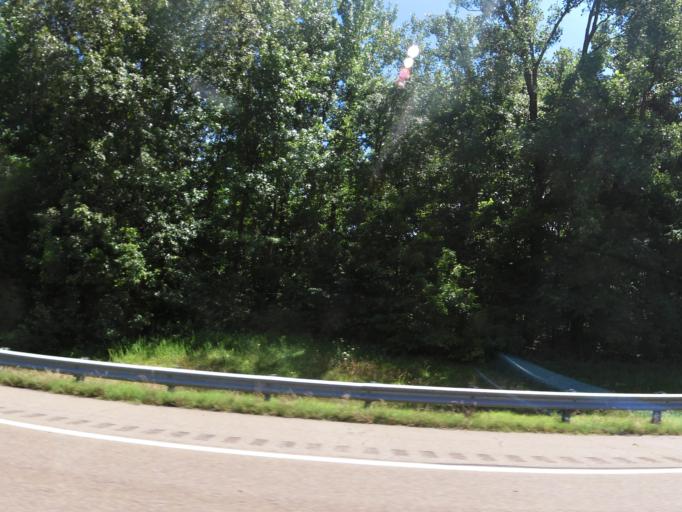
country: US
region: Tennessee
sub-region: Dyer County
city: Dyersburg
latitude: 36.0694
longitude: -89.4372
